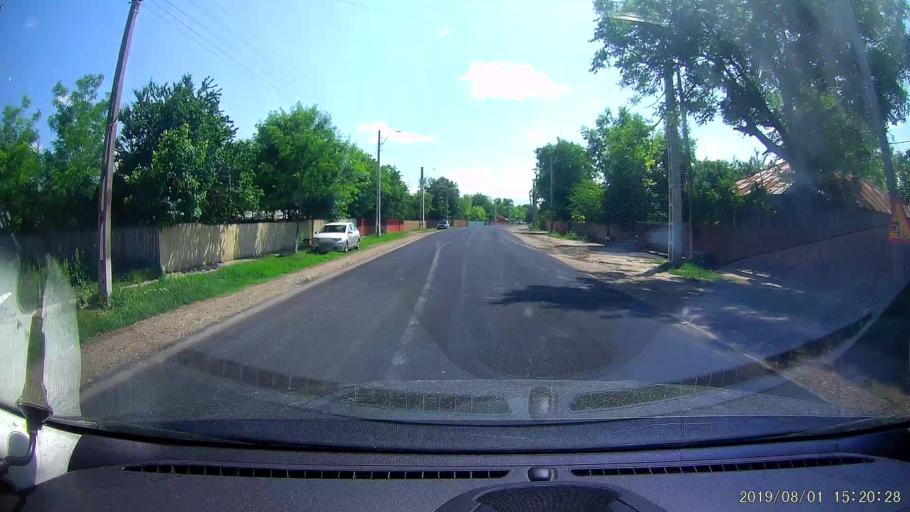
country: RO
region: Braila
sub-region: Comuna Tufesti
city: Tufesti
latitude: 45.0791
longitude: 27.8068
